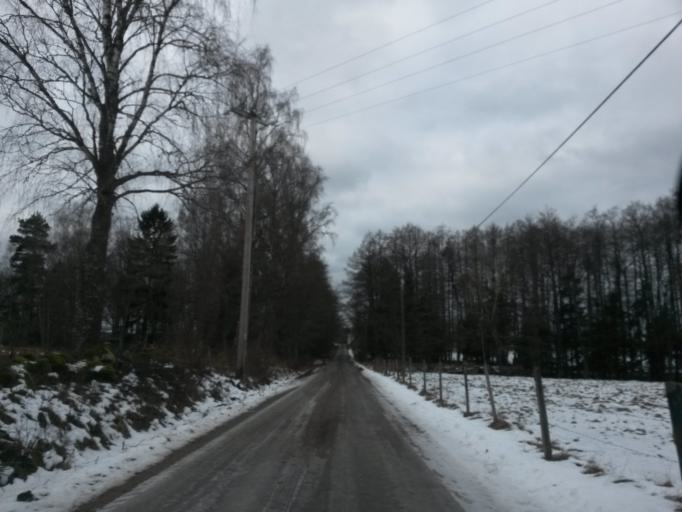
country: SE
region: Vaestra Goetaland
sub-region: Herrljunga Kommun
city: Herrljunga
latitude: 58.0592
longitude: 12.9564
